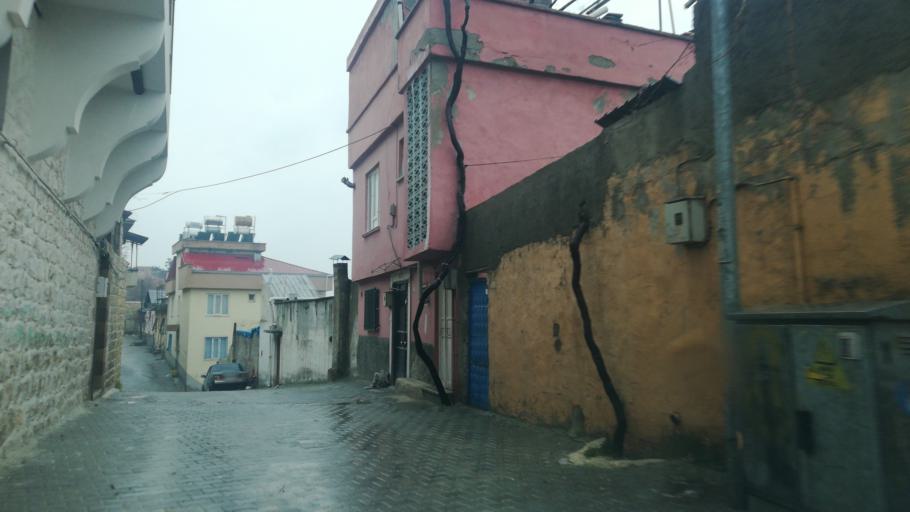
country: TR
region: Kahramanmaras
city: Kahramanmaras
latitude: 37.5862
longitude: 36.9321
